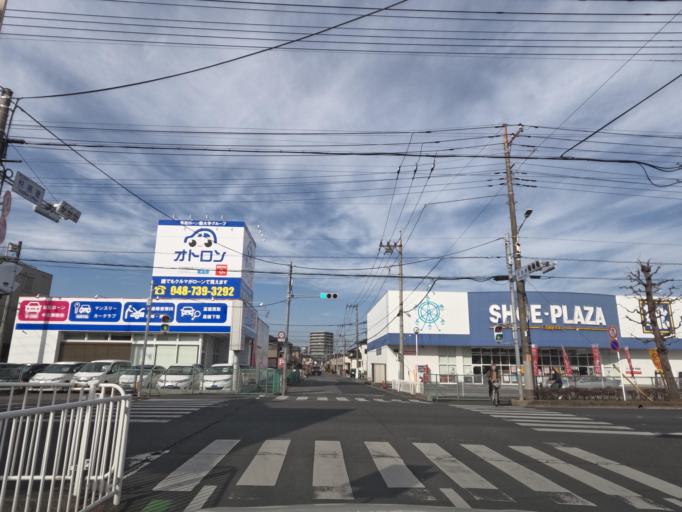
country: JP
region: Saitama
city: Kasukabe
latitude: 35.9690
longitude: 139.7503
